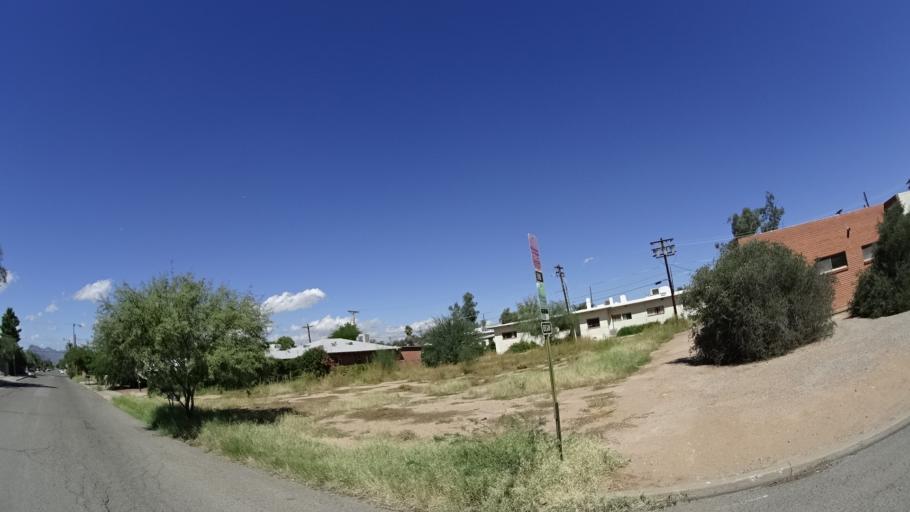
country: US
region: Arizona
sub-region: Pima County
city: Tucson
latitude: 32.2396
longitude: -110.9556
